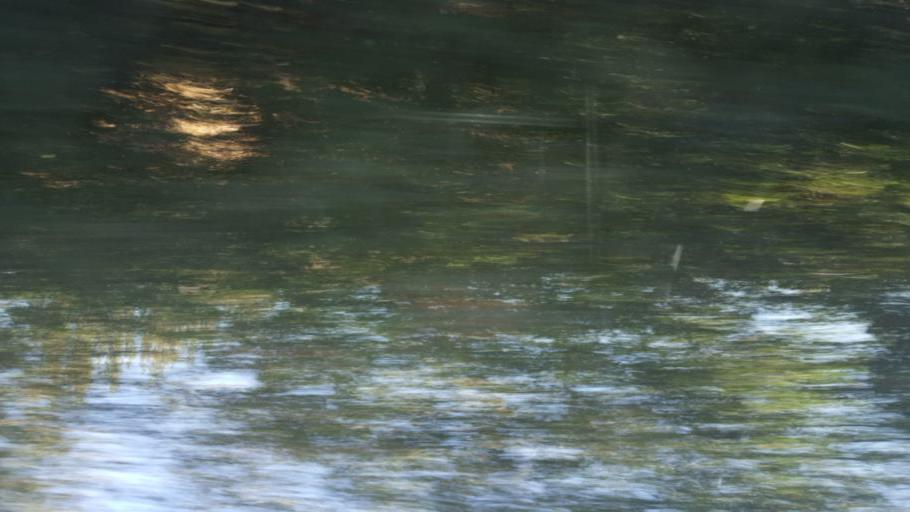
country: TR
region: Ankara
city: Haymana
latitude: 39.3757
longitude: 32.5931
